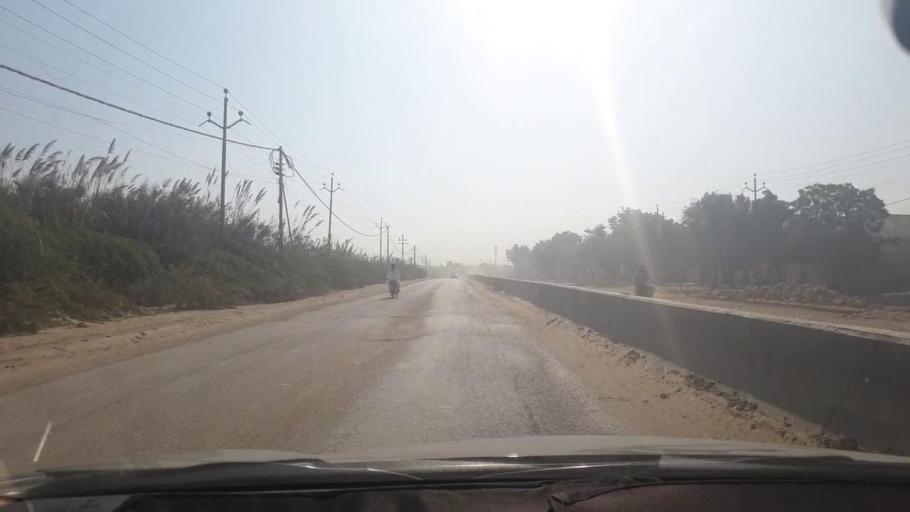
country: PK
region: Sindh
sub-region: Karachi District
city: Karachi
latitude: 25.0044
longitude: 67.0330
